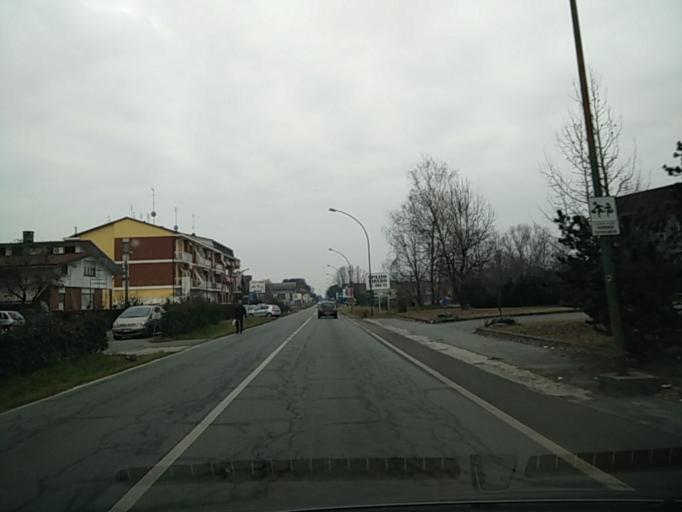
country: IT
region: Piedmont
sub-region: Provincia di Torino
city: Leini
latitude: 45.1969
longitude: 7.7234
